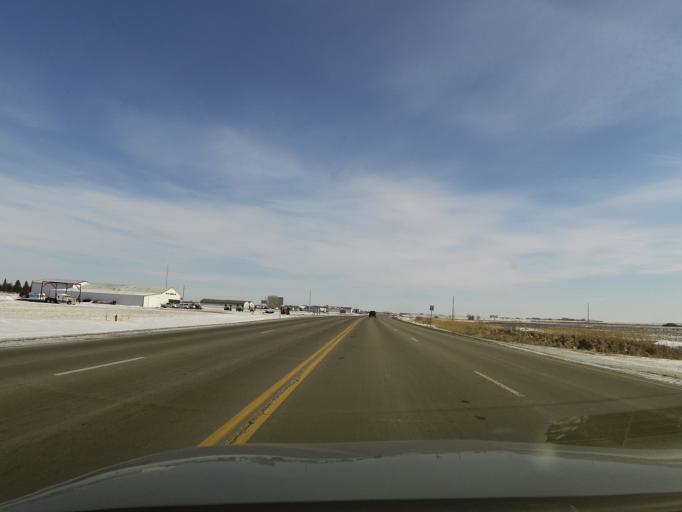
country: US
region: North Dakota
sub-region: Walsh County
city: Grafton
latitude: 48.4124
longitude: -97.3964
